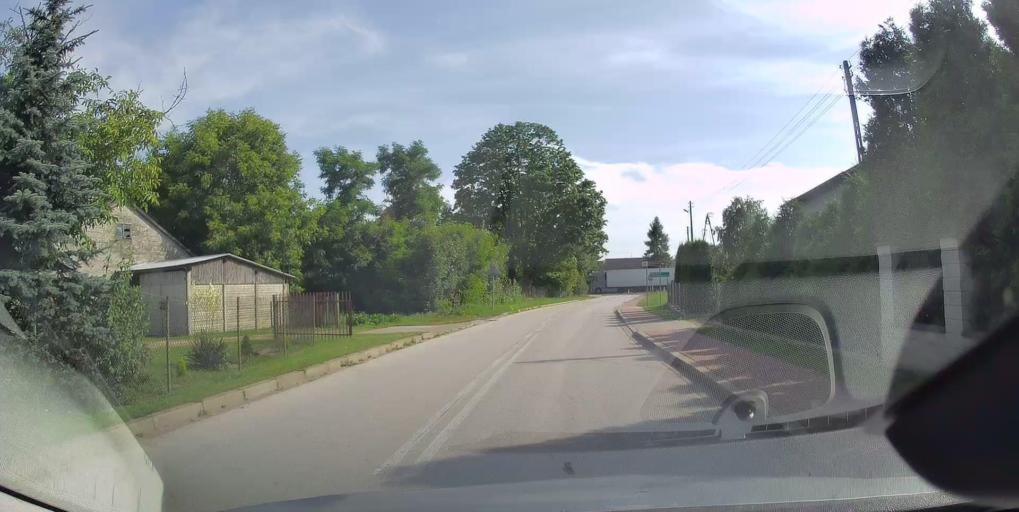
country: PL
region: Lodz Voivodeship
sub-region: Powiat opoczynski
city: Mniszkow
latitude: 51.3319
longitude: 20.0301
